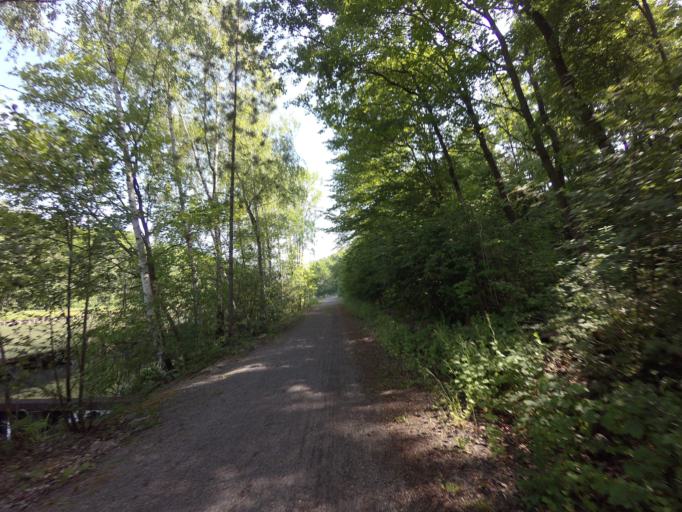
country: DE
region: Lower Saxony
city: Vordorf
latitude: 52.3500
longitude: 10.5444
